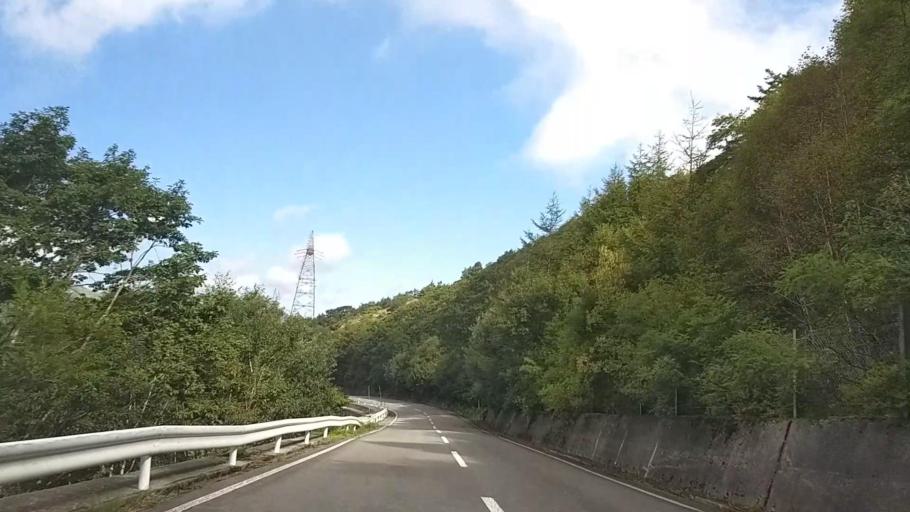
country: JP
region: Nagano
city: Suwa
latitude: 36.1358
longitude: 138.1518
